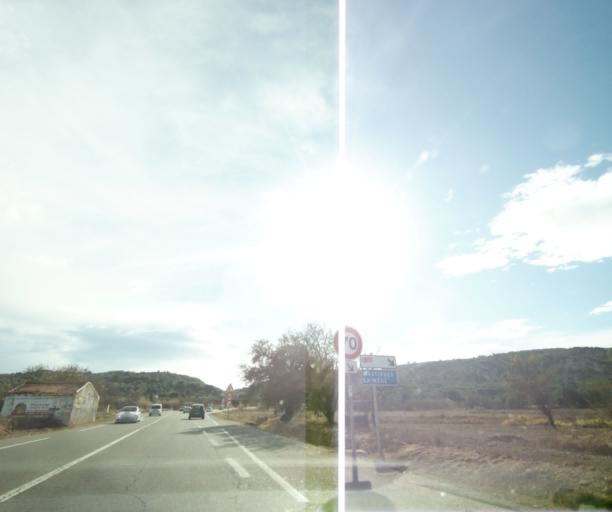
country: FR
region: Provence-Alpes-Cote d'Azur
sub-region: Departement des Bouches-du-Rhone
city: Chateauneuf-les-Martigues
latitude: 43.3763
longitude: 5.1865
